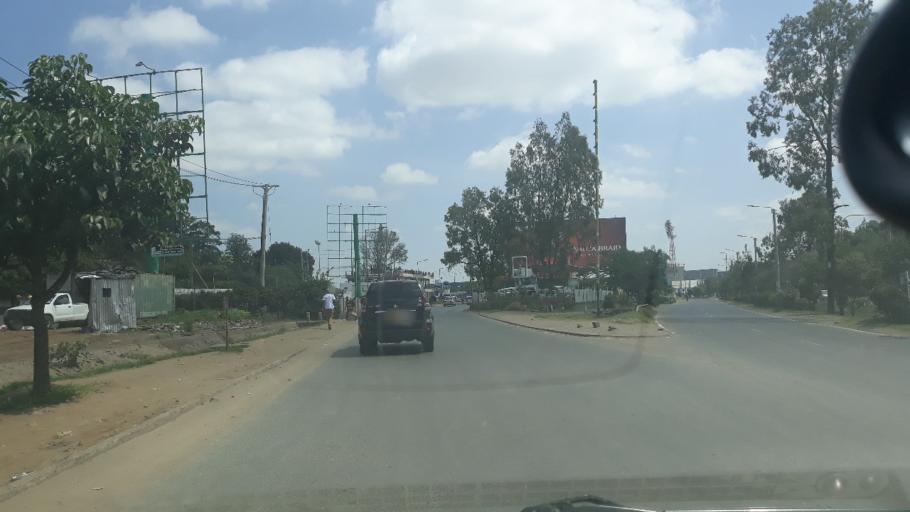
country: KE
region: Nairobi Area
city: Nairobi
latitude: -1.3062
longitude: 36.8204
